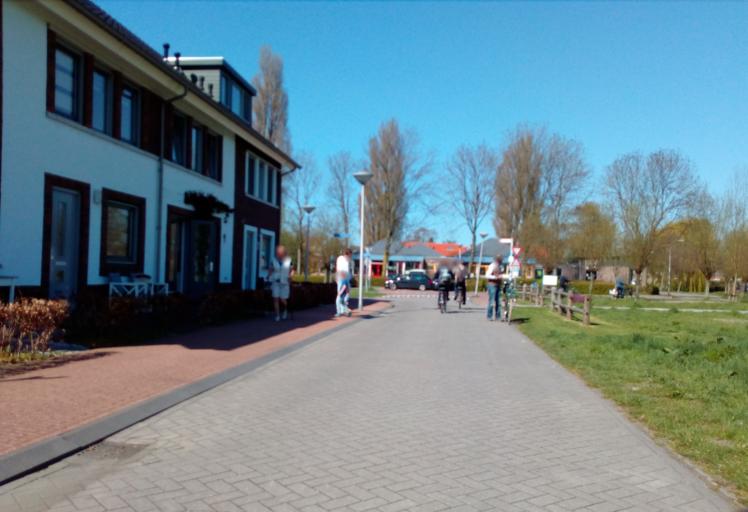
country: NL
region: South Holland
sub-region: Gemeente Delft
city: Delft
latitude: 51.9718
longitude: 4.3146
